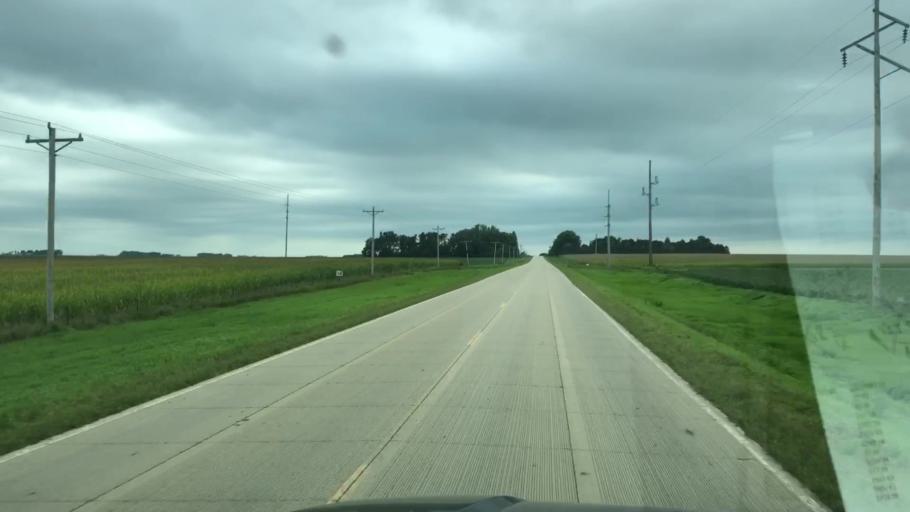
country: US
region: Iowa
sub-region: O'Brien County
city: Sheldon
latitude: 43.1739
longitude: -95.9801
